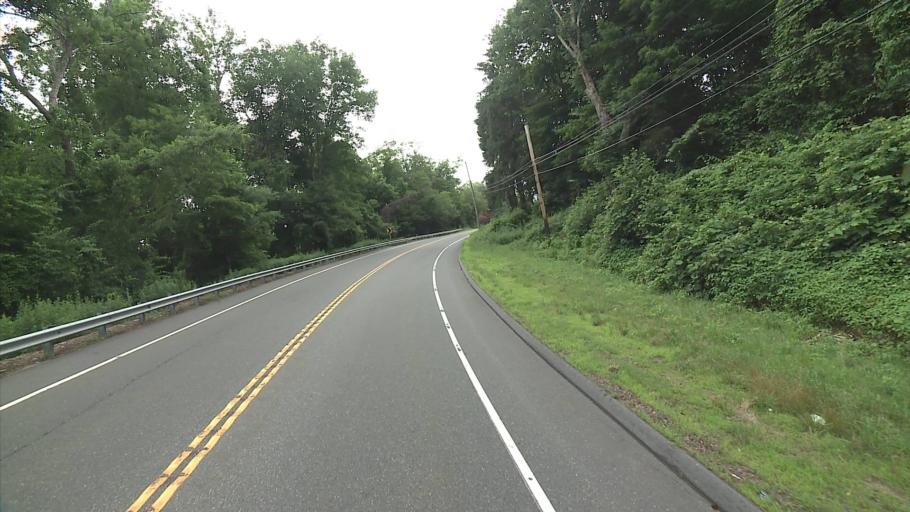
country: US
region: Connecticut
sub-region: New London County
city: Ledyard Center
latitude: 41.4715
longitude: -72.0252
